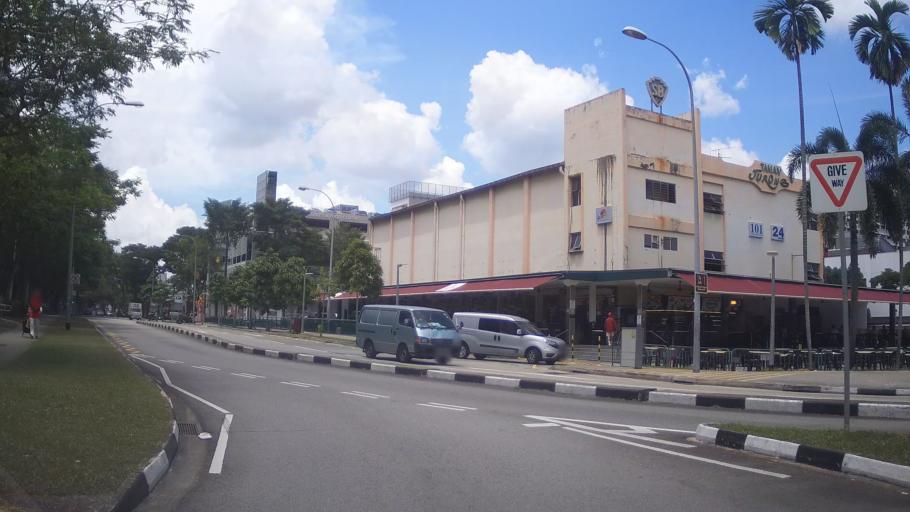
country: SG
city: Singapore
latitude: 1.3340
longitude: 103.7227
